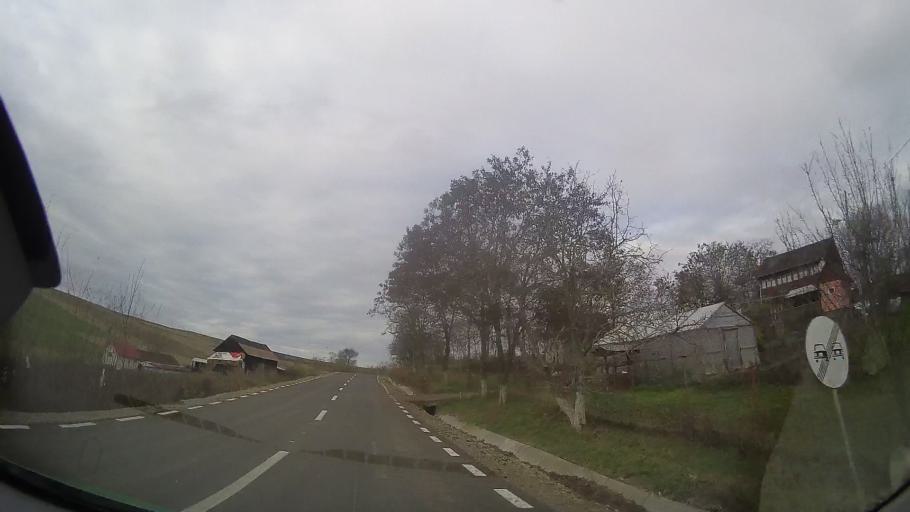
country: RO
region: Bistrita-Nasaud
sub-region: Comuna Teaca
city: Ocnita
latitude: 46.8226
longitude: 24.4829
